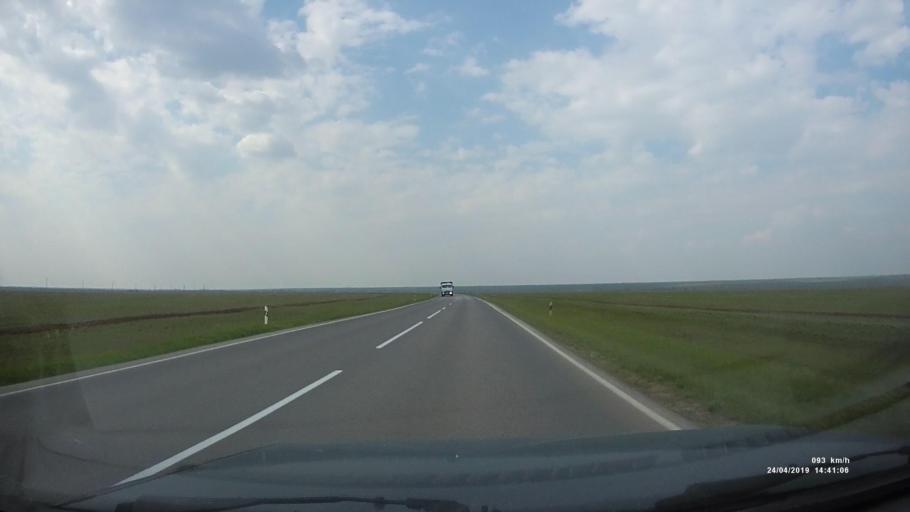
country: RU
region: Rostov
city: Remontnoye
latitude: 46.4410
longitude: 43.8835
